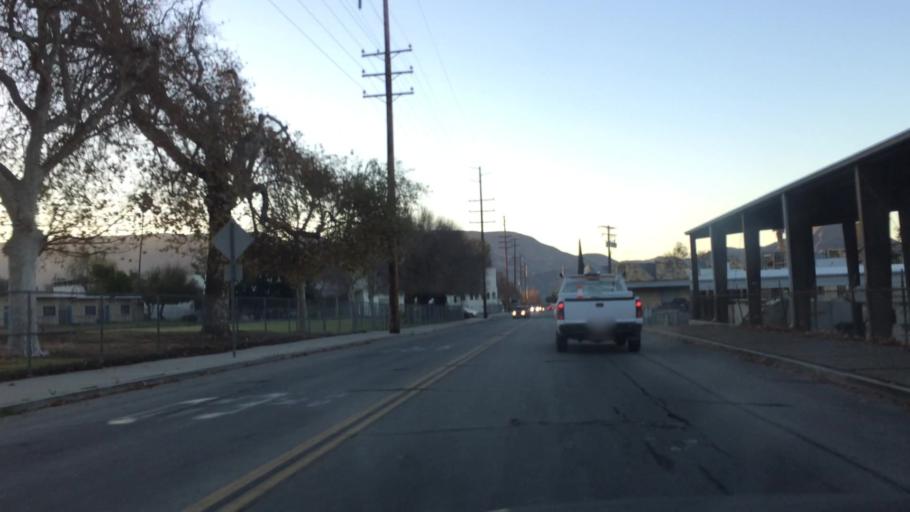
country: US
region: California
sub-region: Ventura County
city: Fillmore
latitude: 34.4012
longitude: -118.9188
